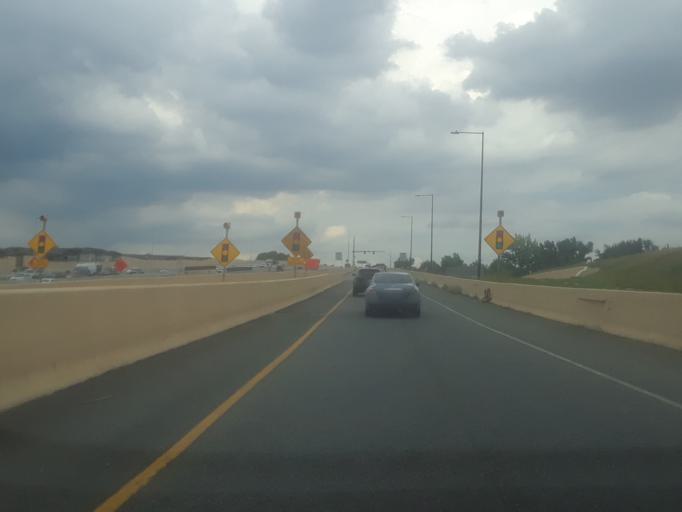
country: US
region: Colorado
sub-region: Arapahoe County
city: Columbine Valley
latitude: 39.5637
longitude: -105.0292
